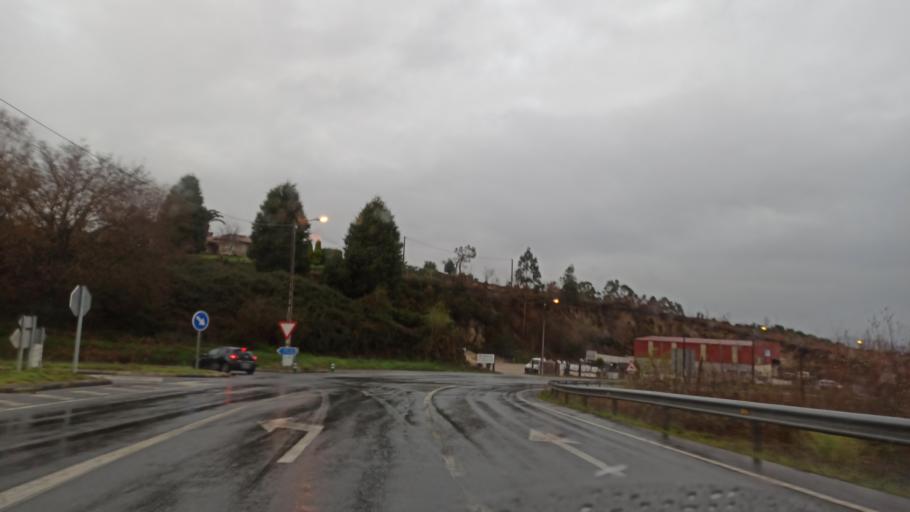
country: ES
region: Galicia
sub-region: Provincia da Coruna
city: Betanzos
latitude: 43.2619
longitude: -8.2073
